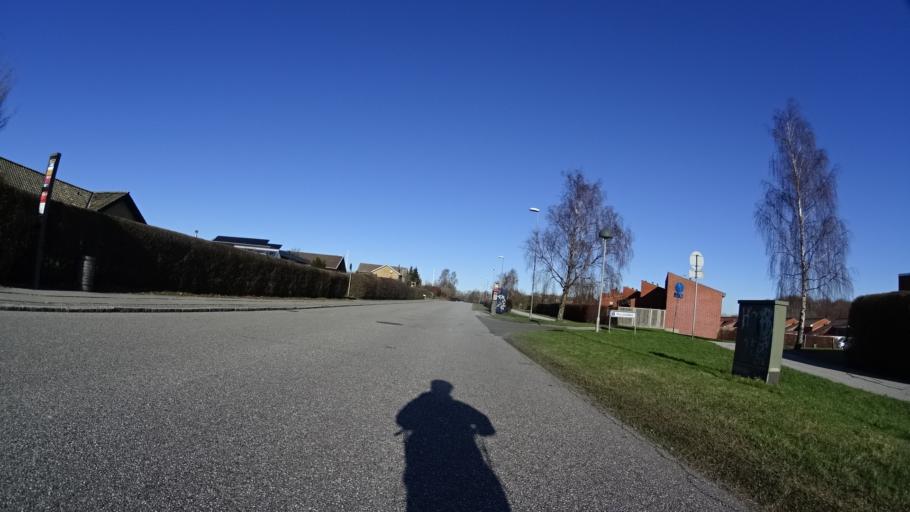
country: DK
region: Central Jutland
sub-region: Arhus Kommune
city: Tranbjerg
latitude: 56.1087
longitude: 10.0987
